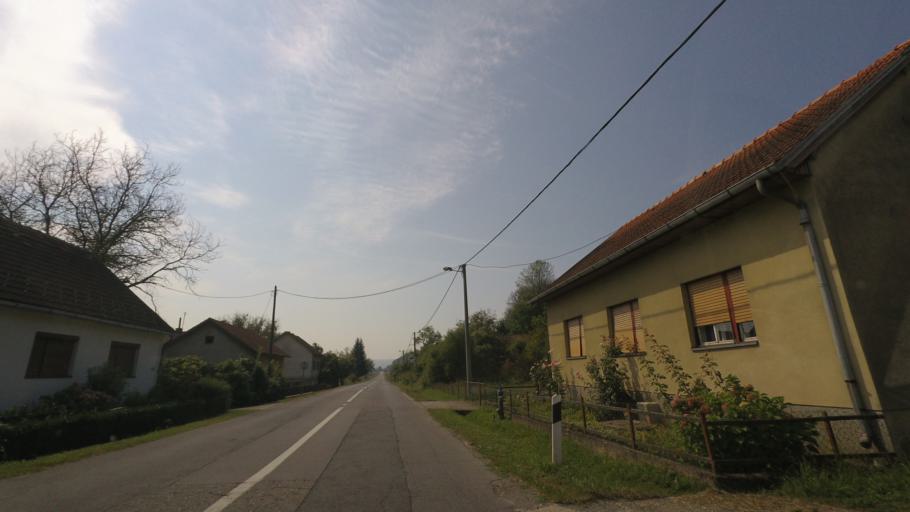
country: HR
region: Sisacko-Moslavacka
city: Dvor
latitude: 45.0859
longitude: 16.3830
